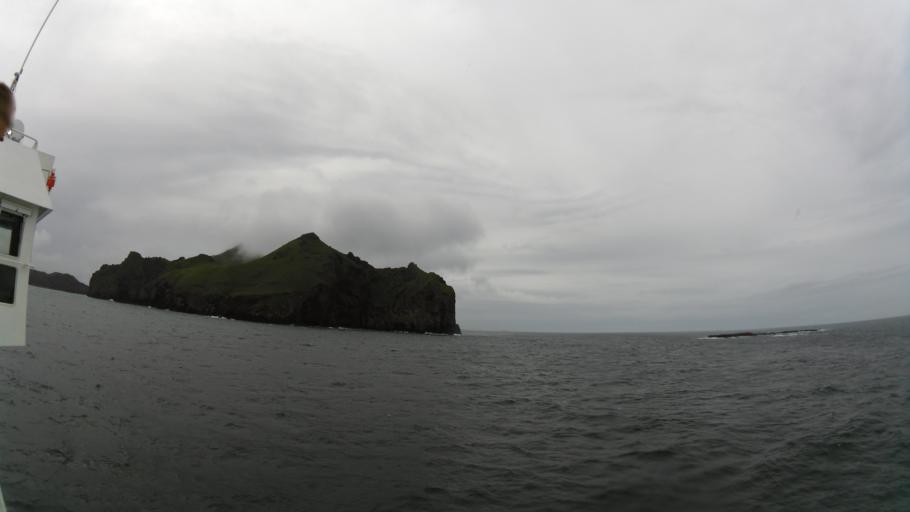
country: IS
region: South
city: Vestmannaeyjar
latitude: 63.4550
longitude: -20.2275
